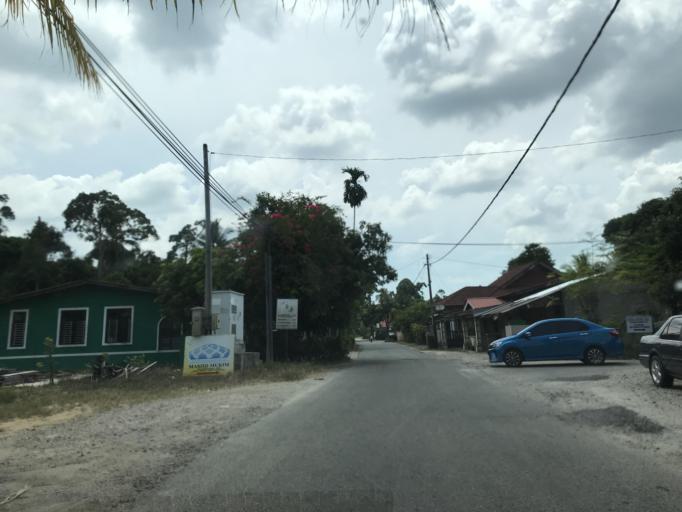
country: MY
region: Kelantan
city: Kota Bharu
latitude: 6.1341
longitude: 102.1822
